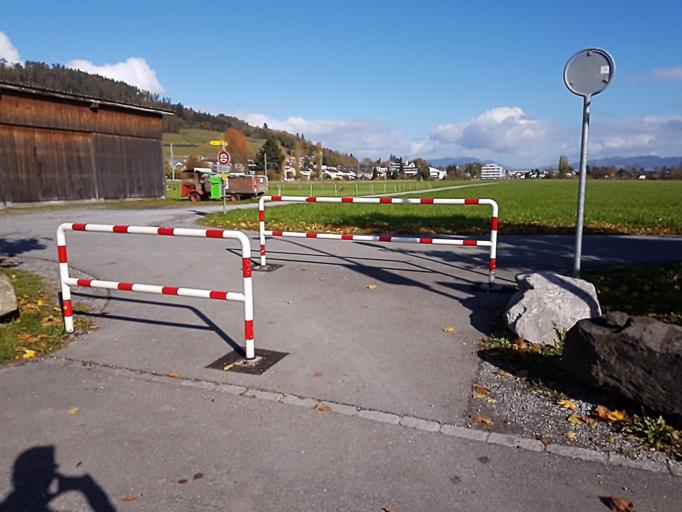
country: CH
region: Appenzell Innerrhoden
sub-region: Appenzell Inner Rhodes
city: Balgach
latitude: 47.4026
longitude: 9.6123
